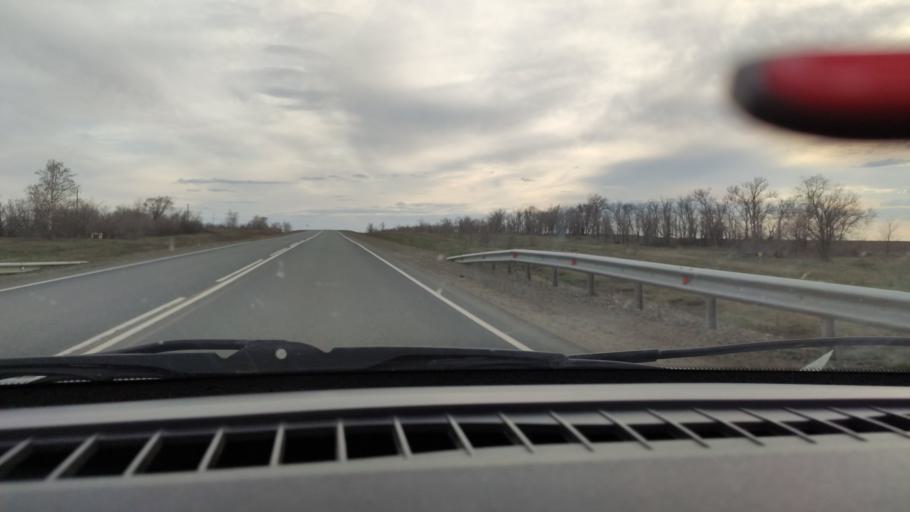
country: RU
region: Orenburg
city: Sakmara
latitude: 52.2771
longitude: 55.3953
